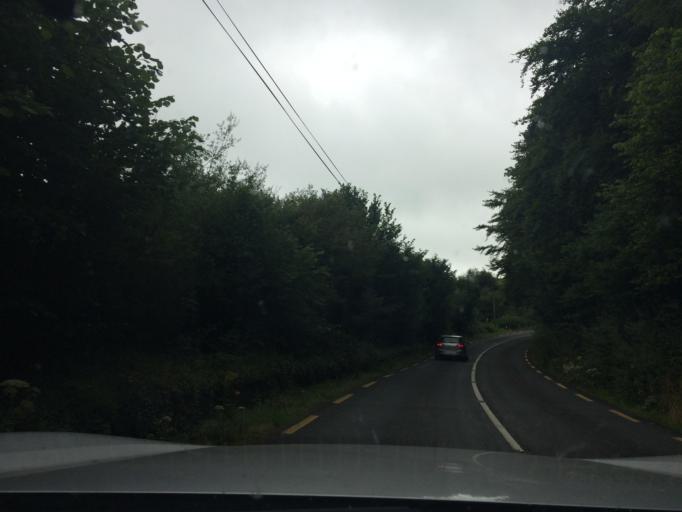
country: IE
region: Munster
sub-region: South Tipperary
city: Cluain Meala
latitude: 52.2515
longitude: -7.7128
